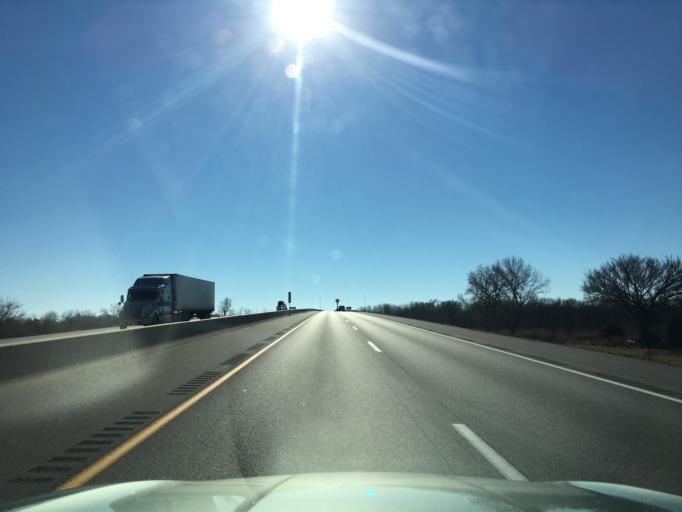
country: US
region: Kansas
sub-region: Sumner County
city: Belle Plaine
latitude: 37.3773
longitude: -97.3235
